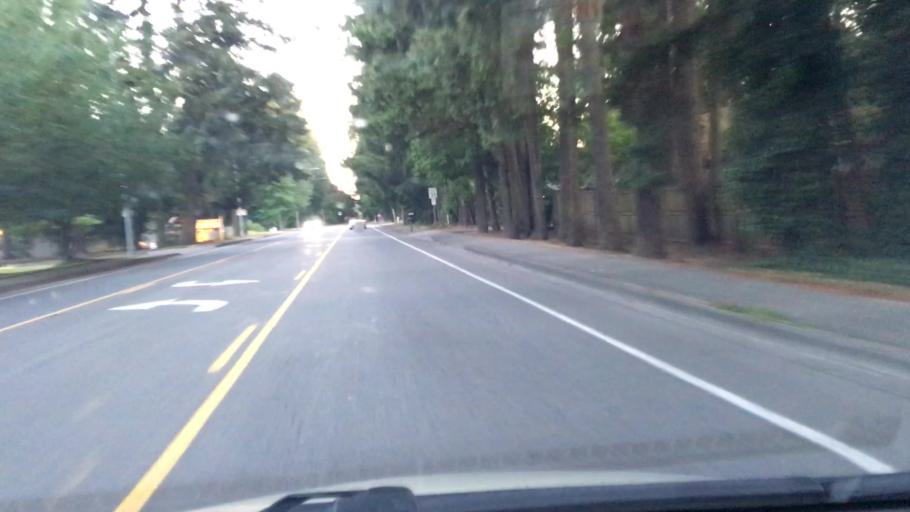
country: US
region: Washington
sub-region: King County
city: Kingsgate
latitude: 47.7300
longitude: -122.1980
